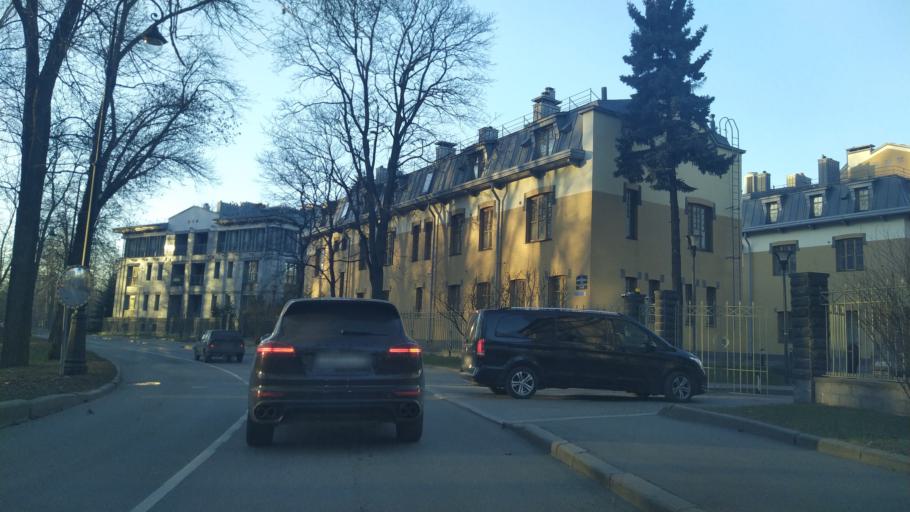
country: RU
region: St.-Petersburg
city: Novaya Derevnya
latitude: 59.9805
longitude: 30.2900
